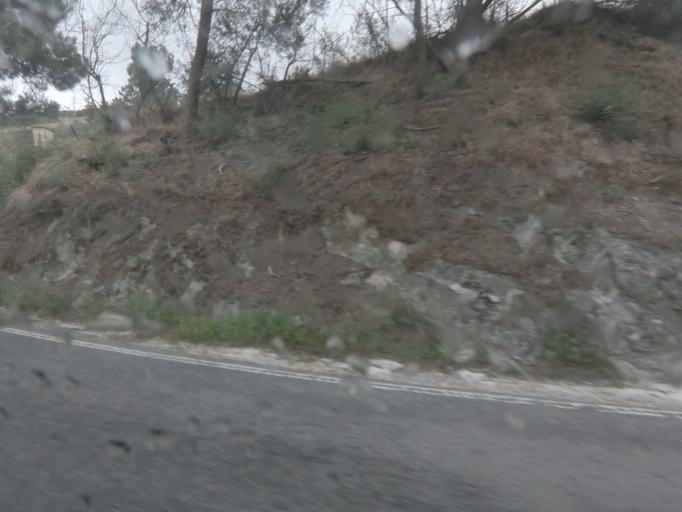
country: PT
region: Viseu
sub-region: Armamar
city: Armamar
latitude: 41.1274
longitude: -7.7342
